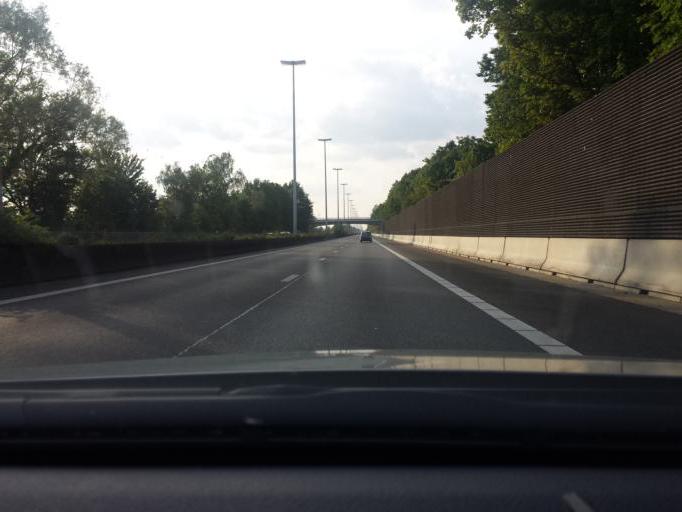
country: BE
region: Flanders
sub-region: Provincie Limburg
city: Hasselt
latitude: 50.9231
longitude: 5.3140
